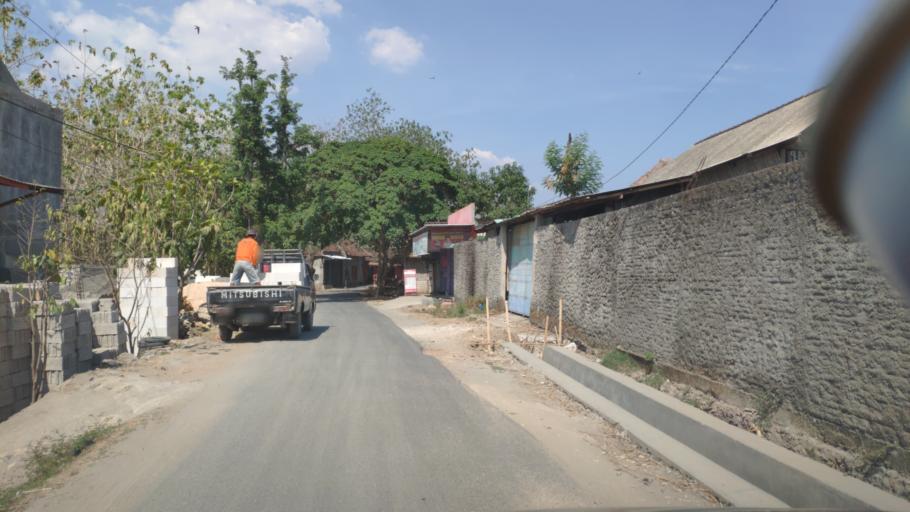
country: ID
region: Central Java
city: Pipes
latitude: -7.0705
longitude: 111.2868
